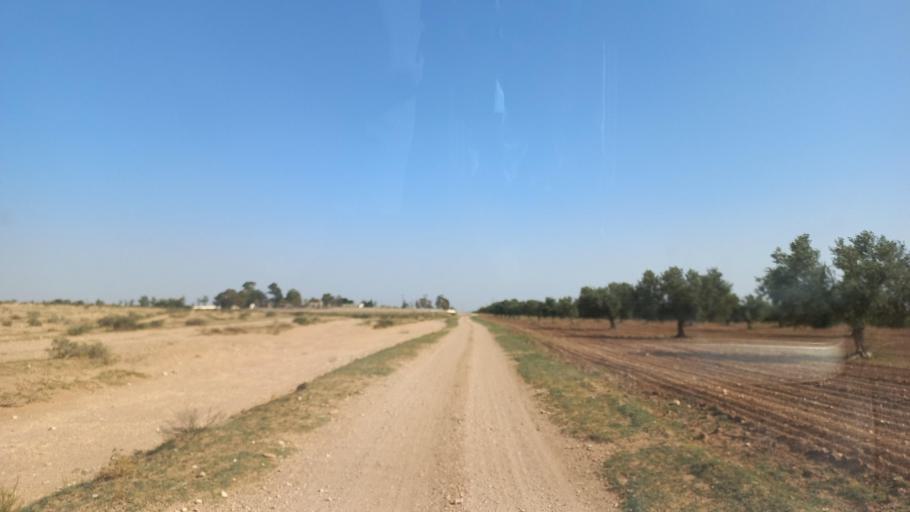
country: TN
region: Al Qasrayn
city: Kasserine
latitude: 35.2996
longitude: 9.0283
